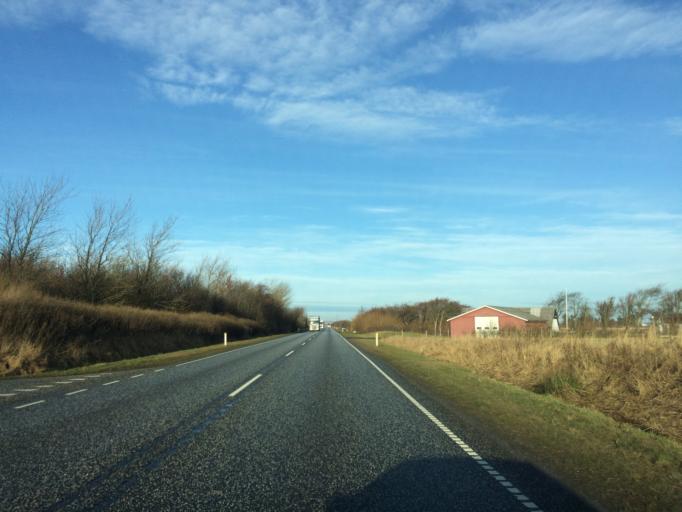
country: DK
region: Central Jutland
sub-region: Struer Kommune
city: Struer
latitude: 56.5457
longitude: 8.5597
